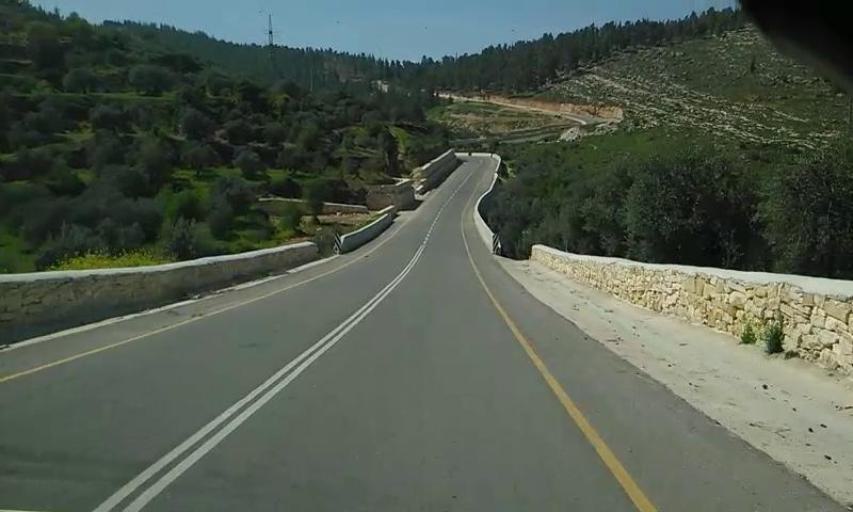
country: PS
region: West Bank
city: Nahhalin
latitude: 31.6800
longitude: 35.1121
